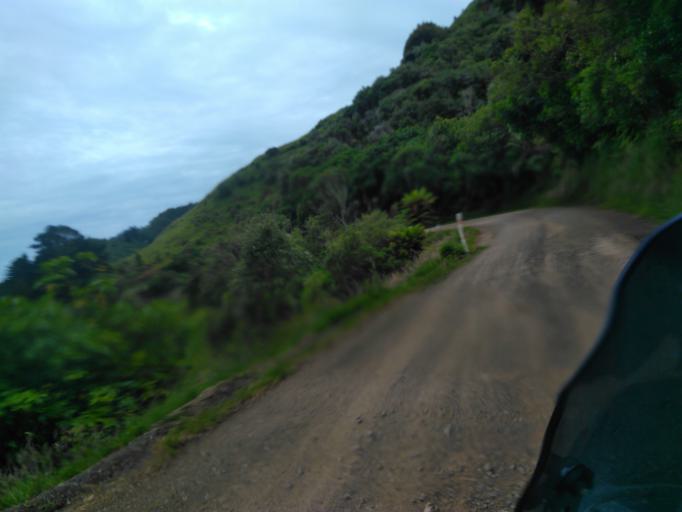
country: NZ
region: Bay of Plenty
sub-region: Opotiki District
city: Opotiki
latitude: -38.1062
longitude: 177.4997
